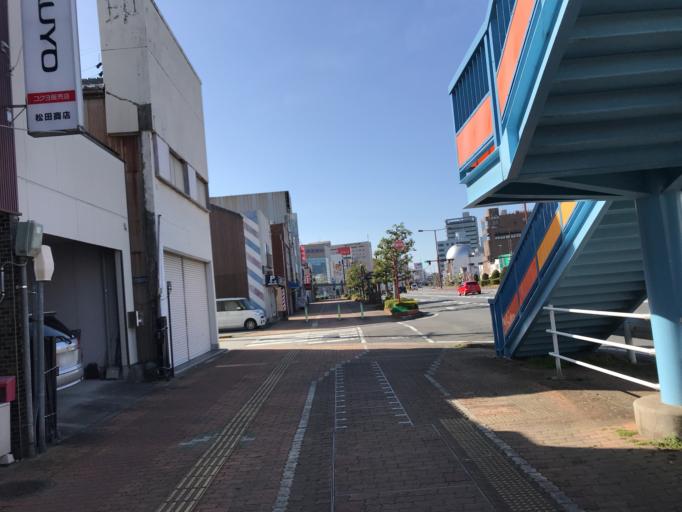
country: JP
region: Mie
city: Tsu-shi
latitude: 34.7230
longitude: 136.5113
